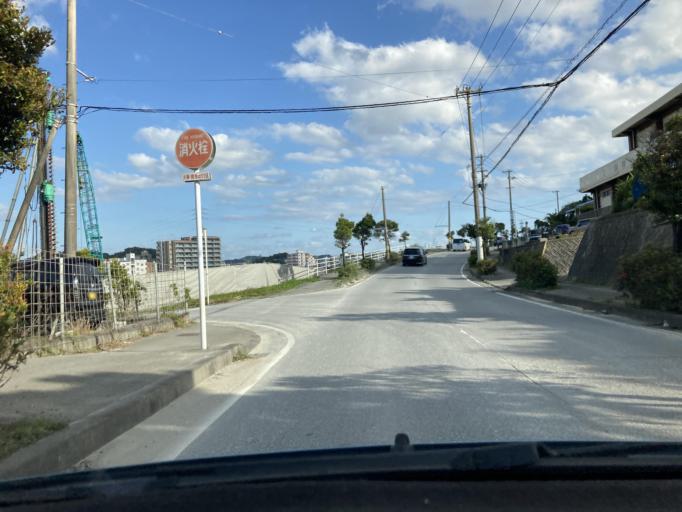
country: JP
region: Okinawa
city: Tomigusuku
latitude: 26.1895
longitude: 127.7053
